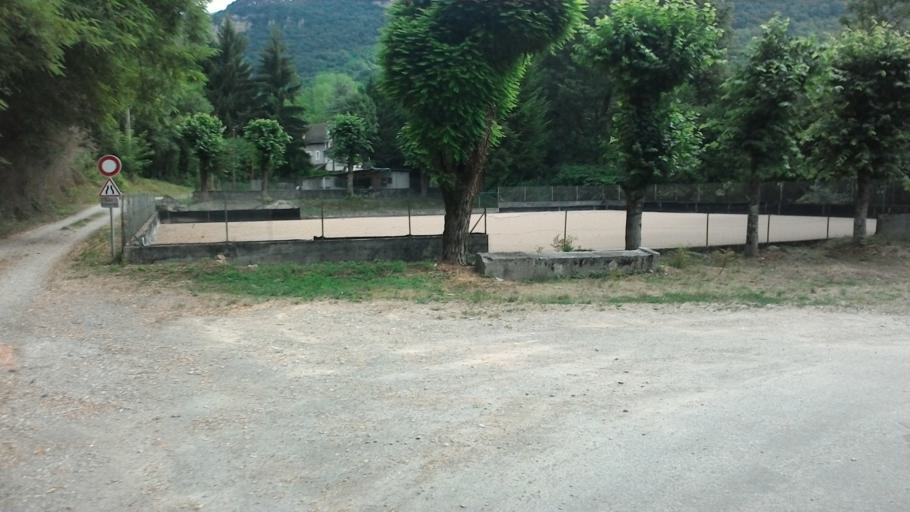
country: FR
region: Rhone-Alpes
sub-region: Departement de l'Ain
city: Villebois
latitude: 45.8461
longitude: 5.4305
